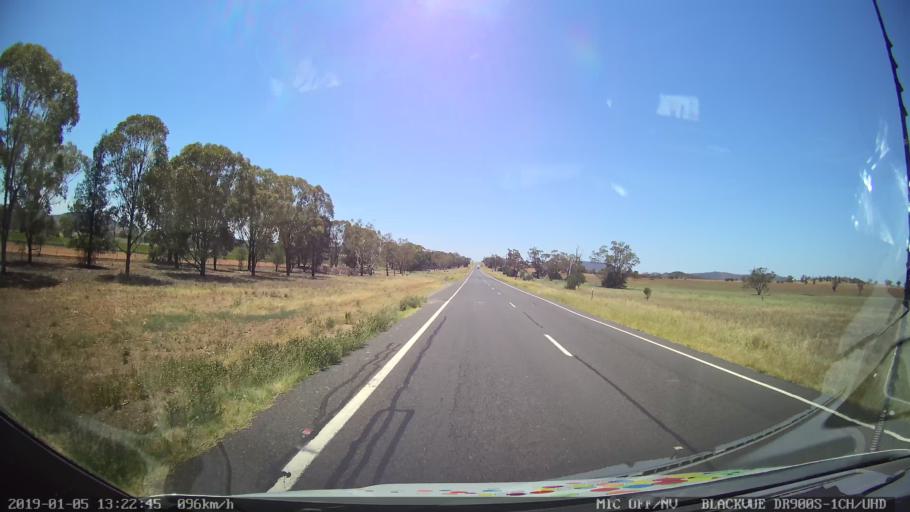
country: AU
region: New South Wales
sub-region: Gunnedah
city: Gunnedah
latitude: -31.0836
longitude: 149.9661
